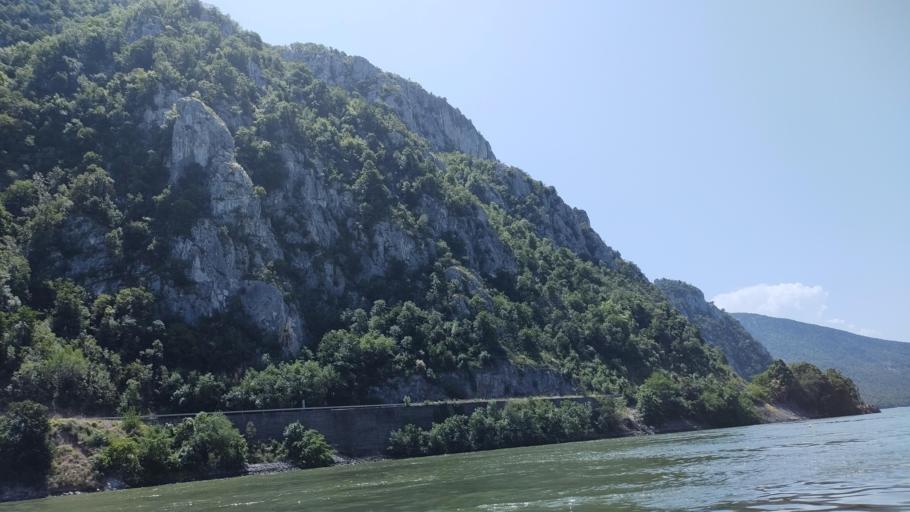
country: RO
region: Mehedinti
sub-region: Comuna Dubova
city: Dubova
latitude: 44.6215
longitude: 22.2748
